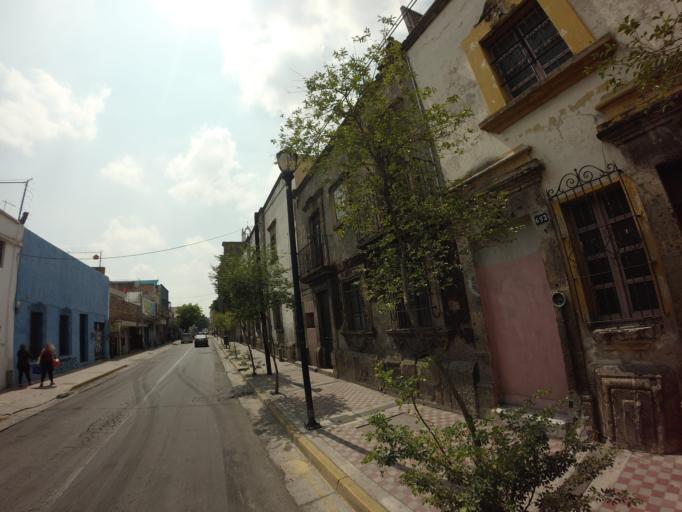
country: MX
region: Jalisco
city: Guadalajara
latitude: 20.6787
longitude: -103.3522
